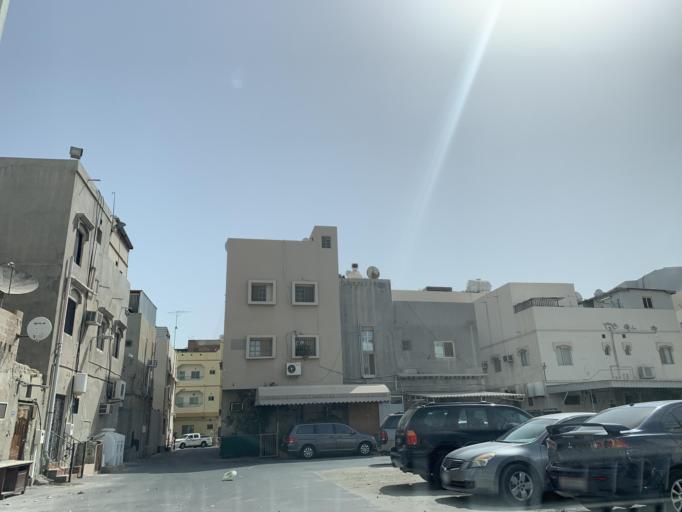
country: BH
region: Manama
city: Manama
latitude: 26.2072
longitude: 50.5874
